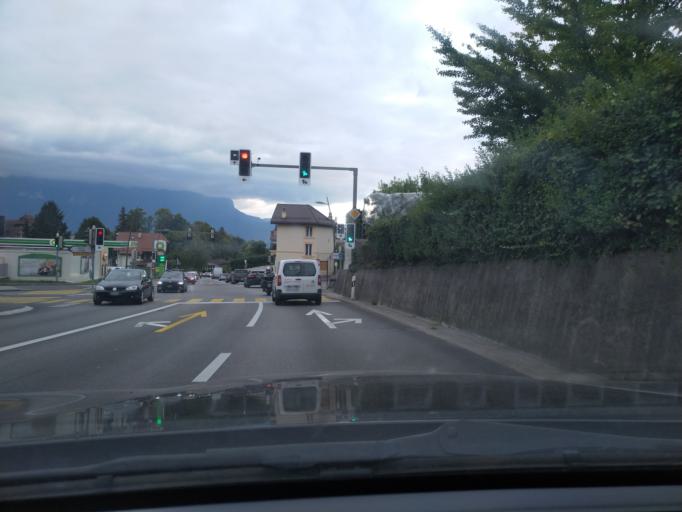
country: CH
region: Vaud
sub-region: Riviera-Pays-d'Enhaut District
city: Jongny
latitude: 46.4715
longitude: 6.8409
